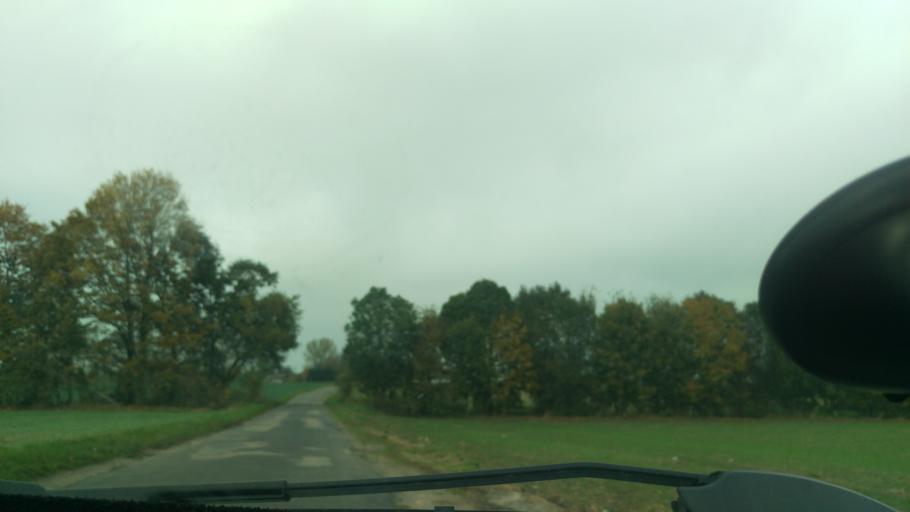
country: PL
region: West Pomeranian Voivodeship
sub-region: Powiat pyrzycki
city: Przelewice
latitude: 53.0696
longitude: 15.1021
